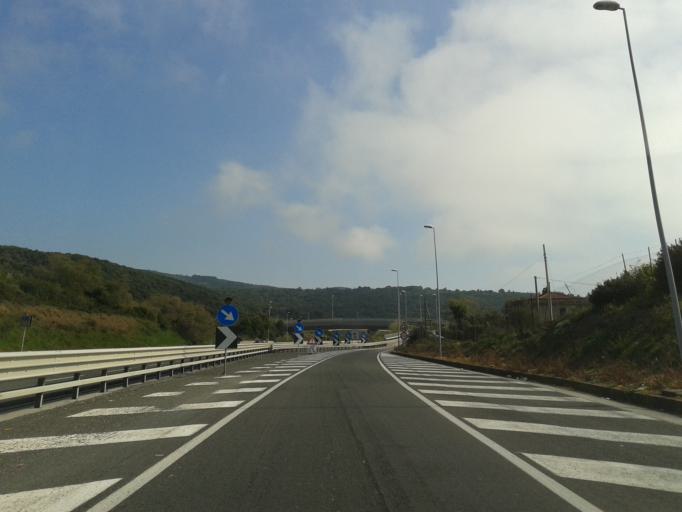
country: IT
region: Tuscany
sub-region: Provincia di Livorno
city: Quercianella
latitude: 43.4856
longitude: 10.3328
